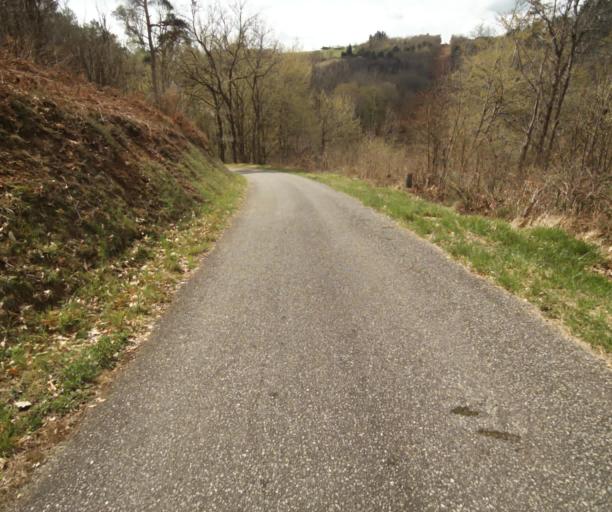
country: FR
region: Limousin
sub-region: Departement de la Correze
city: Sainte-Fortunade
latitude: 45.1854
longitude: 1.8514
